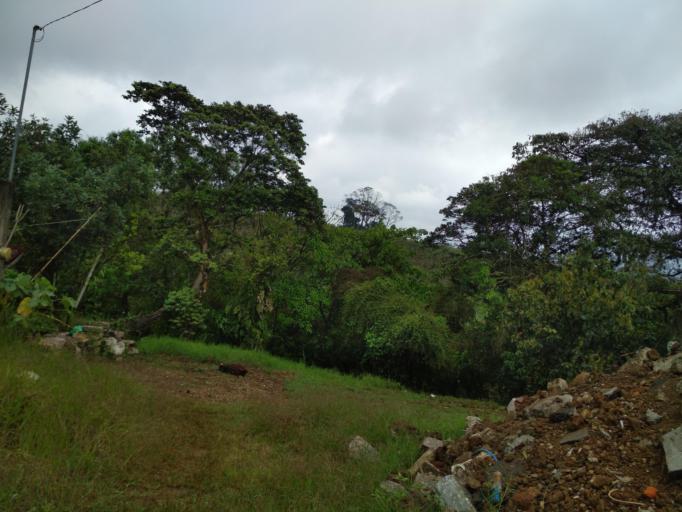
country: MX
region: Veracruz
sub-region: Cordoba
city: San Jose de Tapia
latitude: 18.8508
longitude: -96.9668
